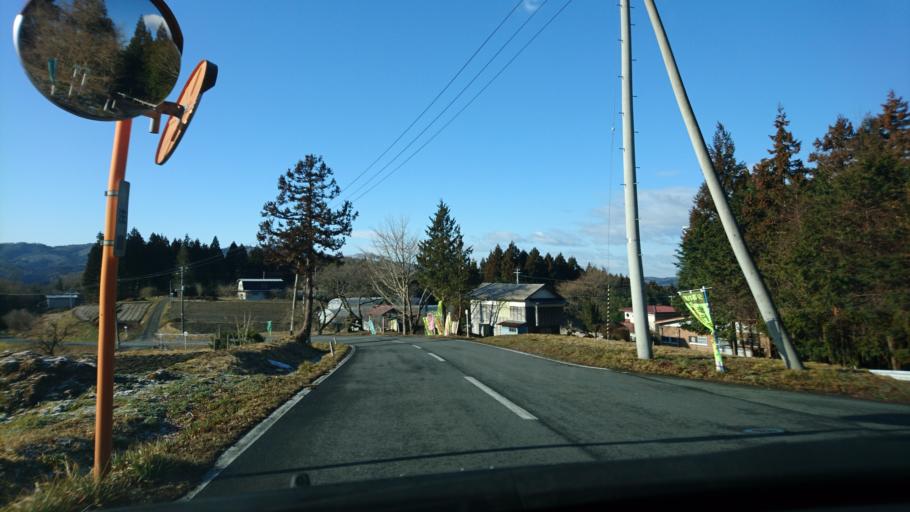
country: JP
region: Iwate
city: Ichinoseki
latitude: 38.8585
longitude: 141.2977
